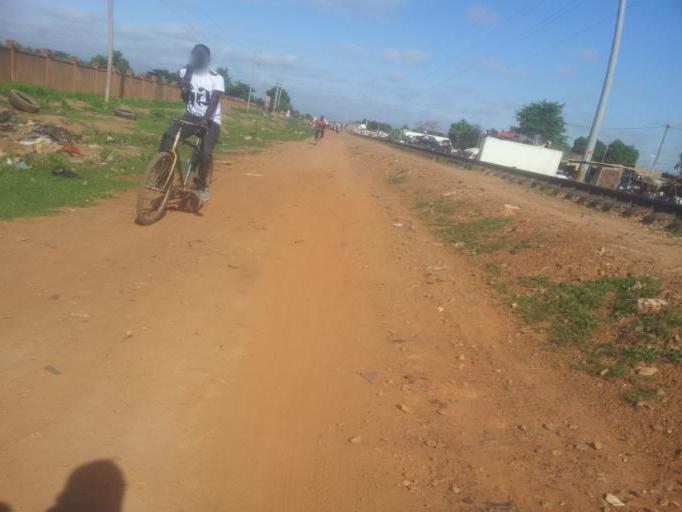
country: BF
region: Centre
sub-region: Kadiogo Province
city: Ouagadougou
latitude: 12.3701
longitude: -1.5566
